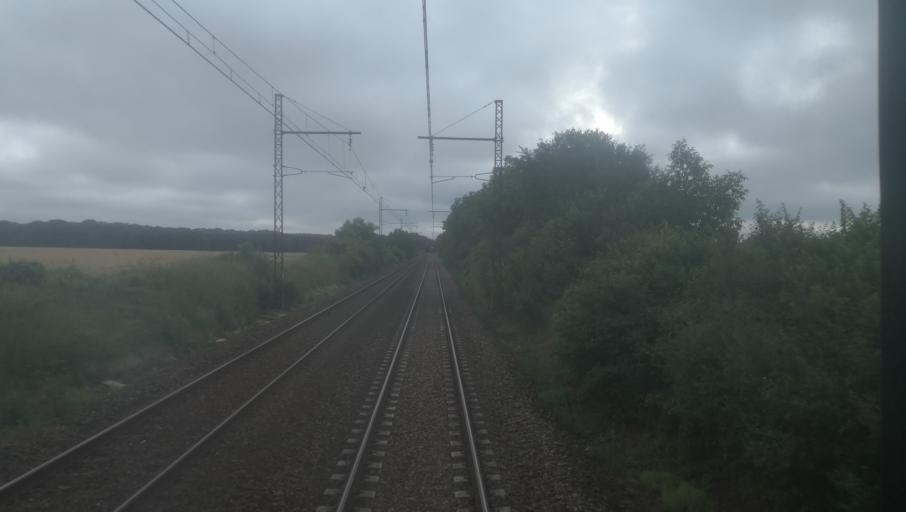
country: FR
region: Centre
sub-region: Departement de l'Indre
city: Montierchaume
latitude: 46.8369
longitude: 1.7631
